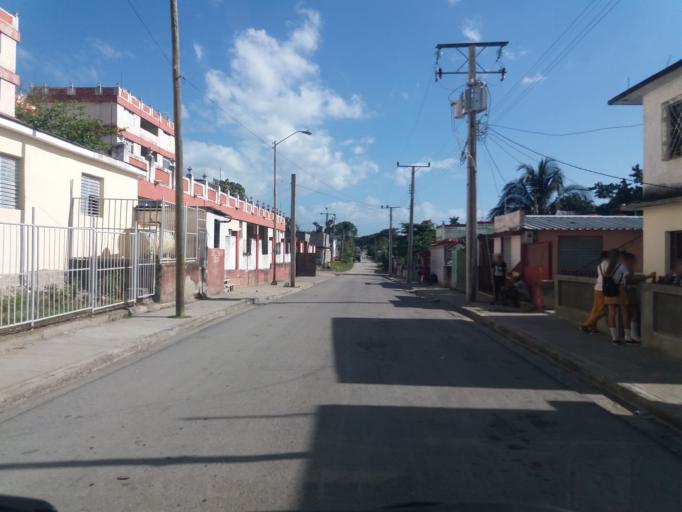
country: CU
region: Cienfuegos
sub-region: Municipio de Cienfuegos
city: Cienfuegos
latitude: 22.1541
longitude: -80.4329
